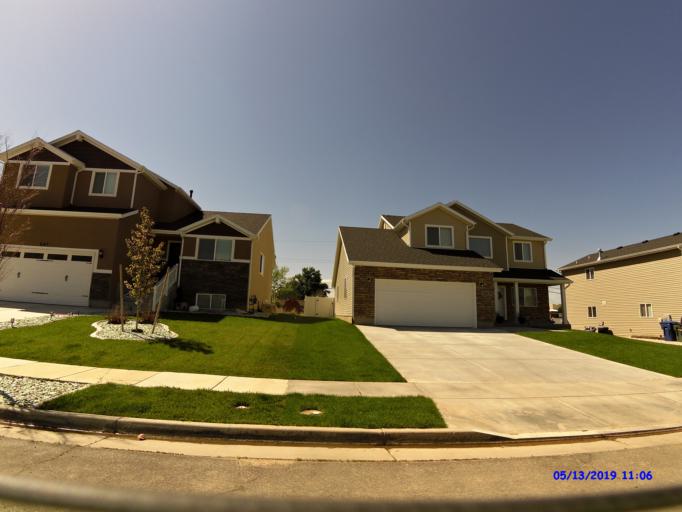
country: US
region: Utah
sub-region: Weber County
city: Harrisville
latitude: 41.2779
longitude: -111.9659
